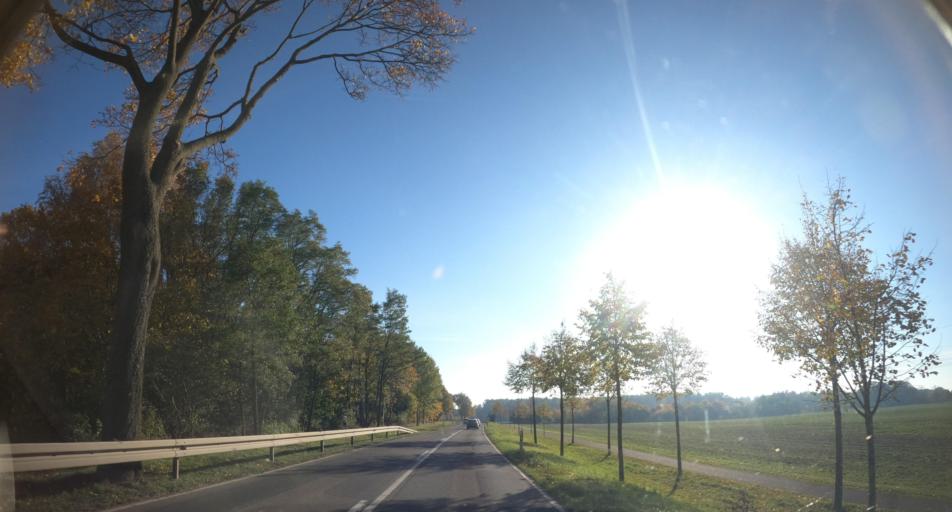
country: DE
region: Mecklenburg-Vorpommern
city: Ueckermunde
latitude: 53.7178
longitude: 14.0641
